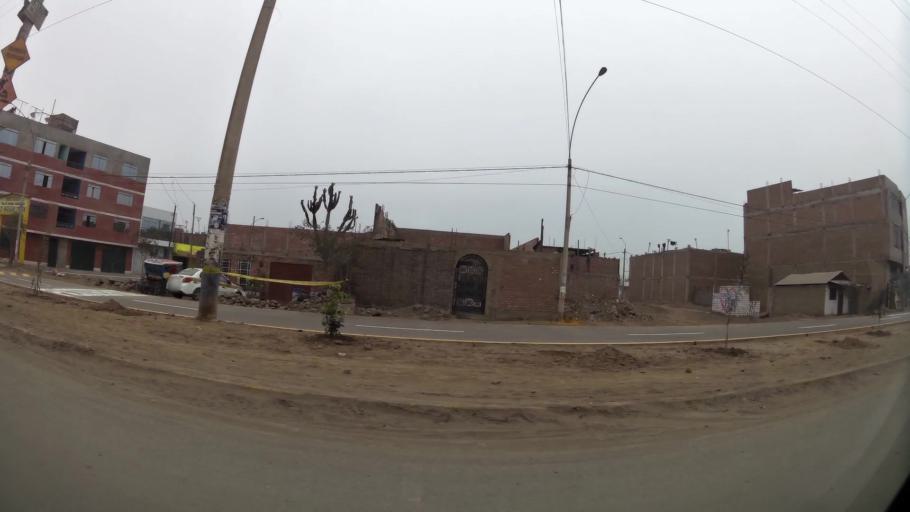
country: PE
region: Lima
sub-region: Lima
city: Urb. Santo Domingo
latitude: -11.8628
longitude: -77.0214
